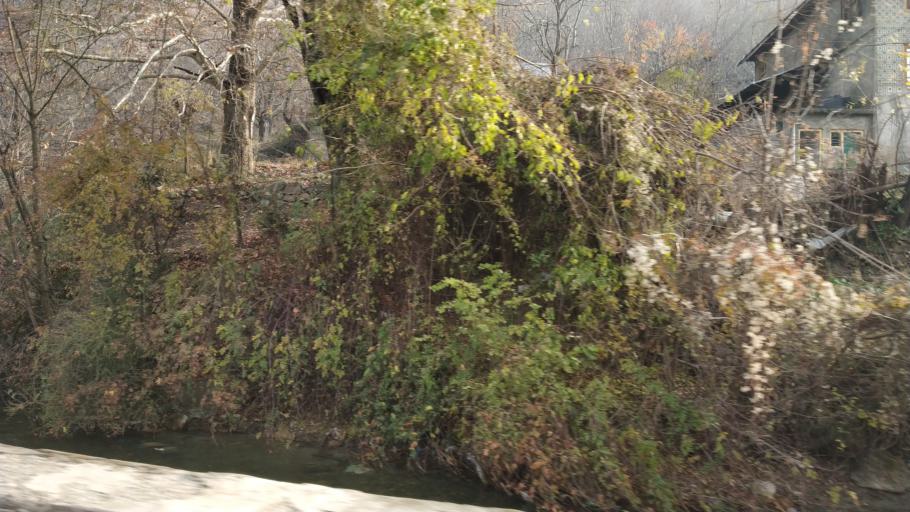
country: IN
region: Kashmir
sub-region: Anantnag
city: Pahalgam
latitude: 33.8675
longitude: 75.2788
